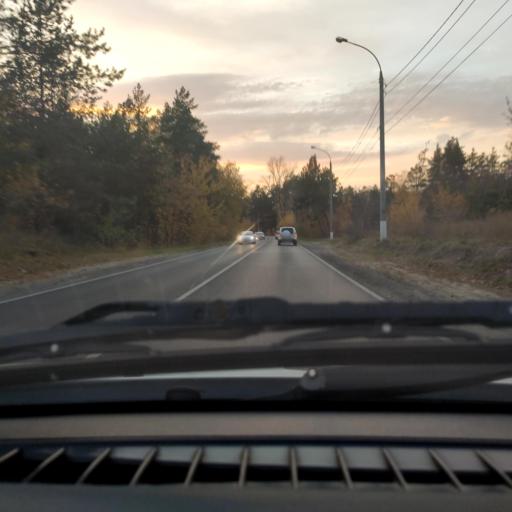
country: RU
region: Samara
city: Zhigulevsk
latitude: 53.4782
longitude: 49.4410
